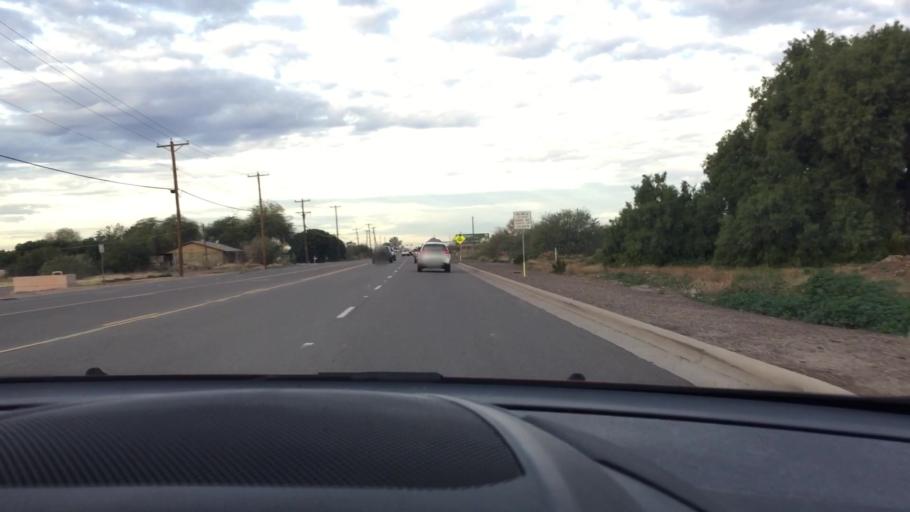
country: US
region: Arizona
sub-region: Maricopa County
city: Mesa
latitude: 33.4654
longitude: -111.8482
